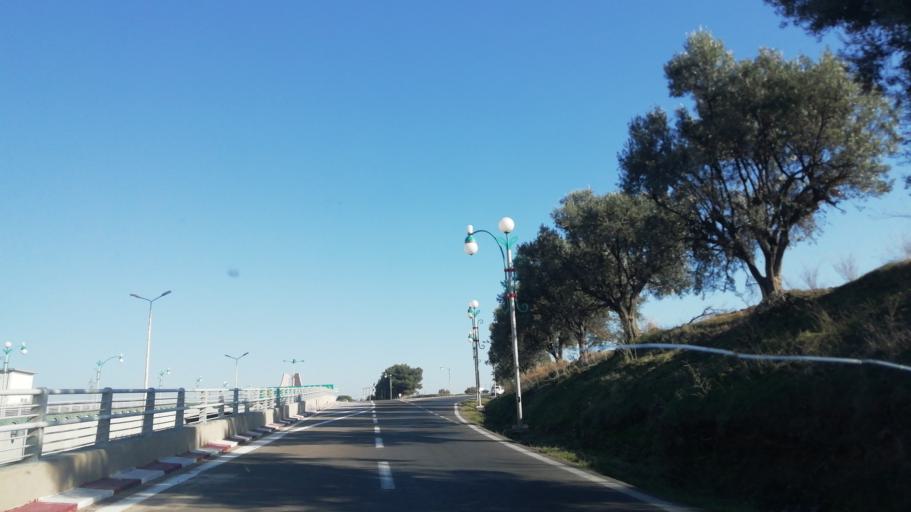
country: DZ
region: Ain Temouchent
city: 'Ain Temouchent
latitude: 35.2999
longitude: -1.1649
